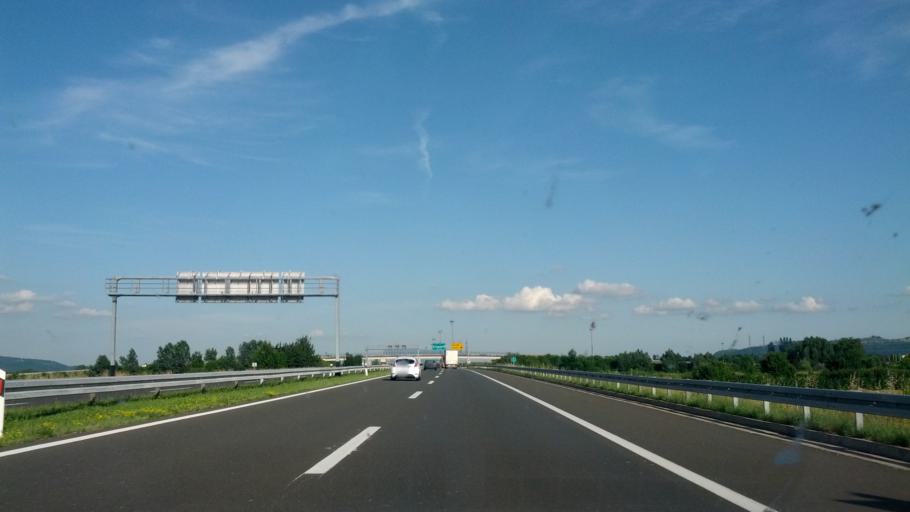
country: HR
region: Zagrebacka
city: Bregana
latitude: 45.8347
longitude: 15.7140
